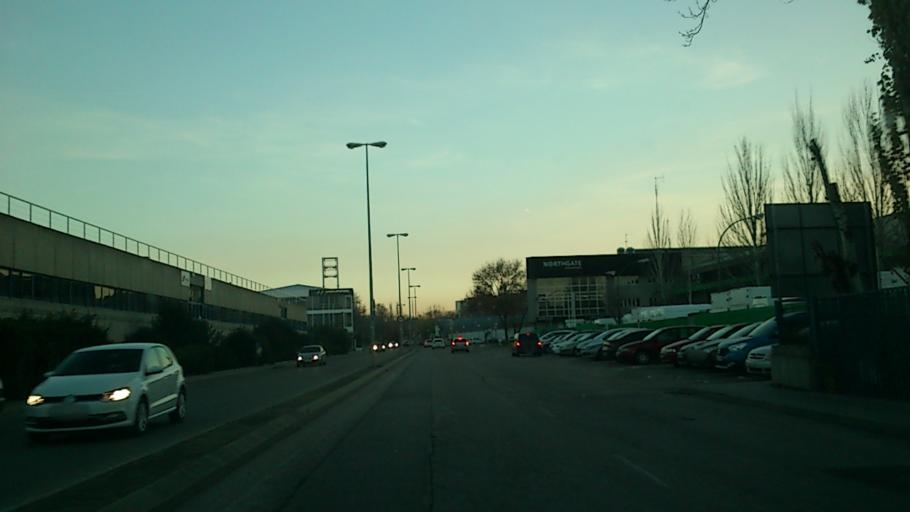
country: ES
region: Madrid
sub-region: Provincia de Madrid
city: San Fernando de Henares
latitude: 40.4367
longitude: -3.5410
